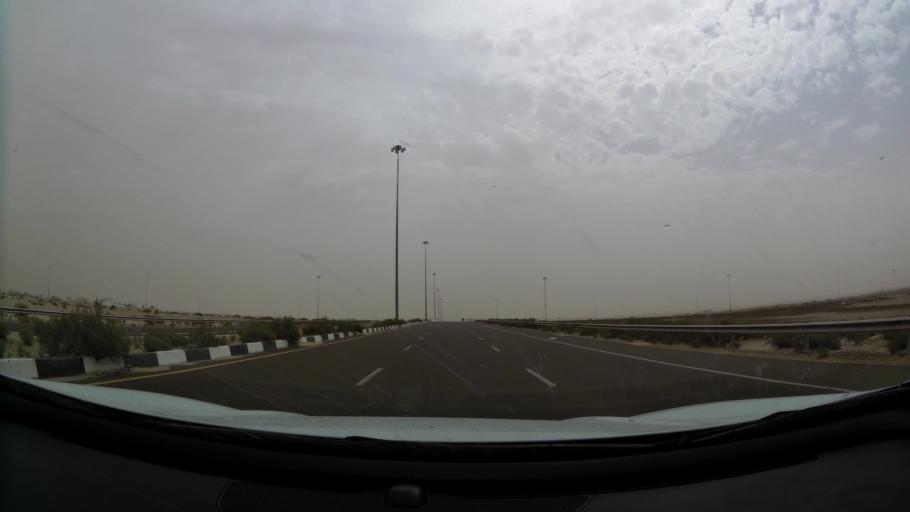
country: AE
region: Abu Dhabi
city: Abu Dhabi
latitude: 24.3784
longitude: 54.7306
